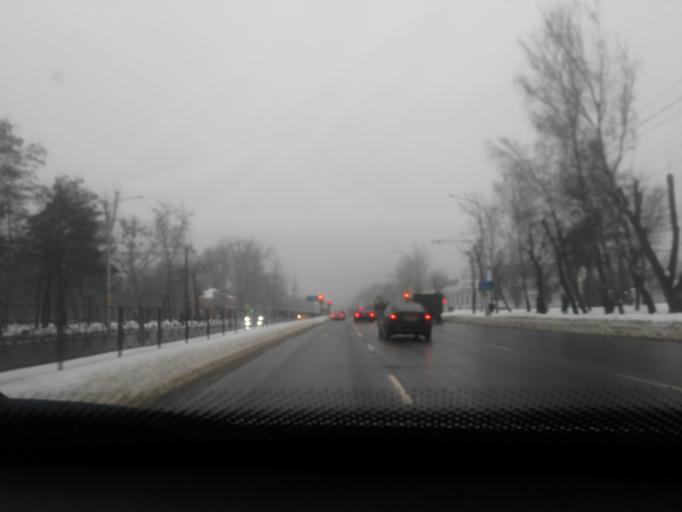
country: BY
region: Mogilev
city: Babruysk
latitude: 53.1657
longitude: 29.2088
